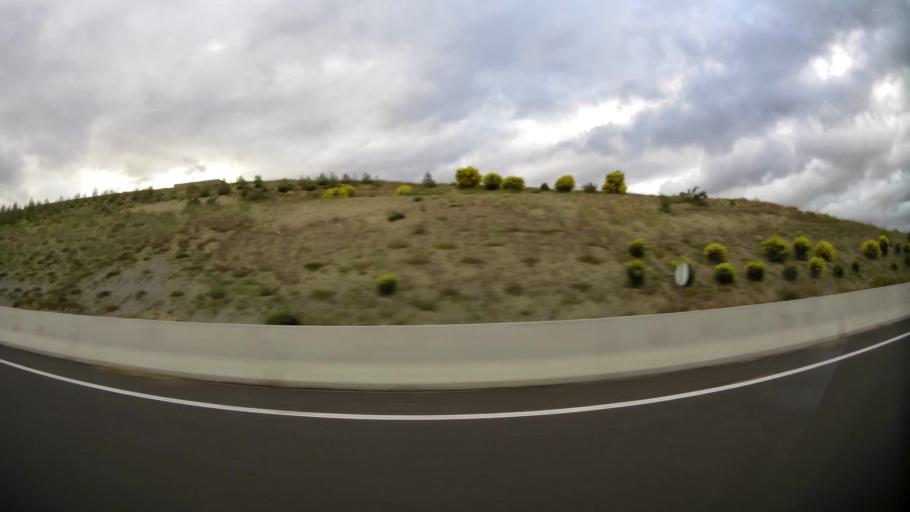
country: MA
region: Taza-Al Hoceima-Taounate
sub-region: Taza
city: Taza
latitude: 34.2538
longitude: -3.8776
